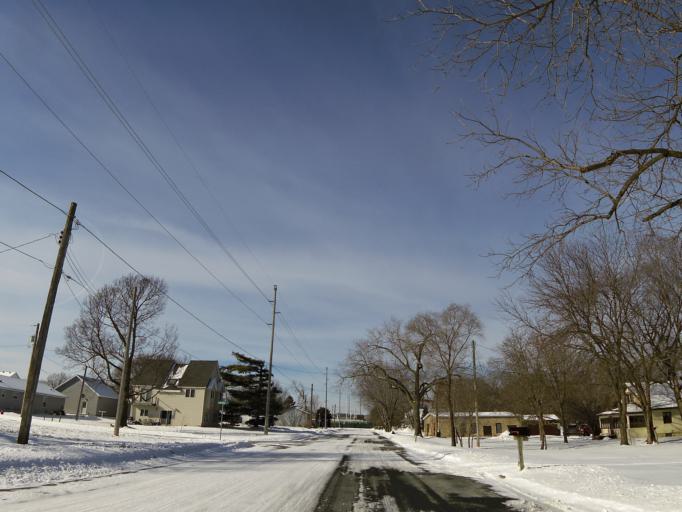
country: US
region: Minnesota
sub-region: Dakota County
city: Hastings
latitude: 44.7455
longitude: -92.8429
